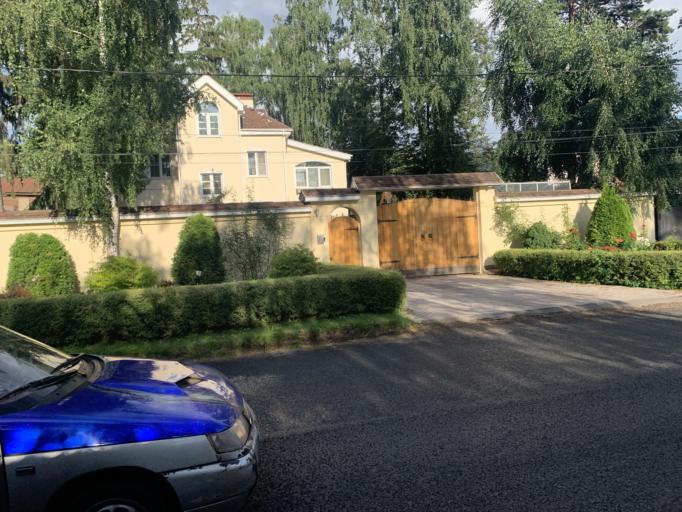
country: RU
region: Moskovskaya
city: Mamontovka
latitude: 55.9747
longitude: 37.8432
